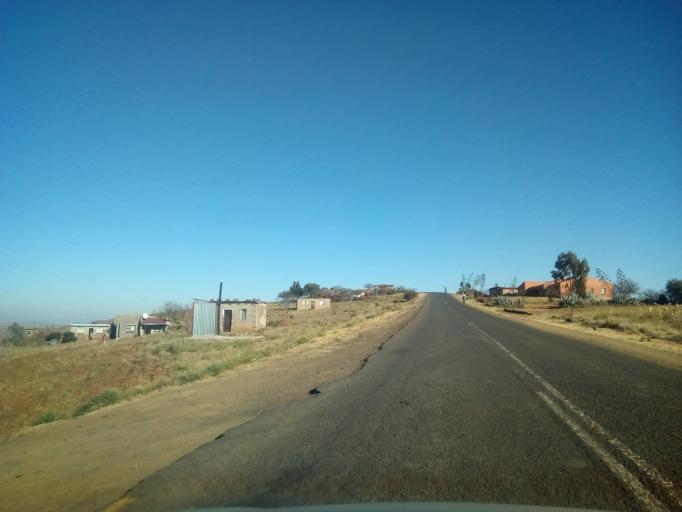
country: LS
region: Berea
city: Teyateyaneng
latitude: -29.2526
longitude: 27.7943
